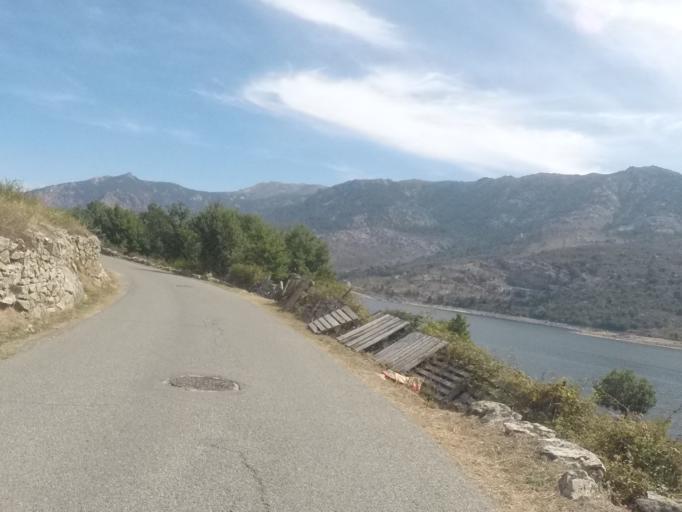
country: FR
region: Corsica
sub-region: Departement de la Haute-Corse
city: Corte
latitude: 42.3289
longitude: 9.0082
